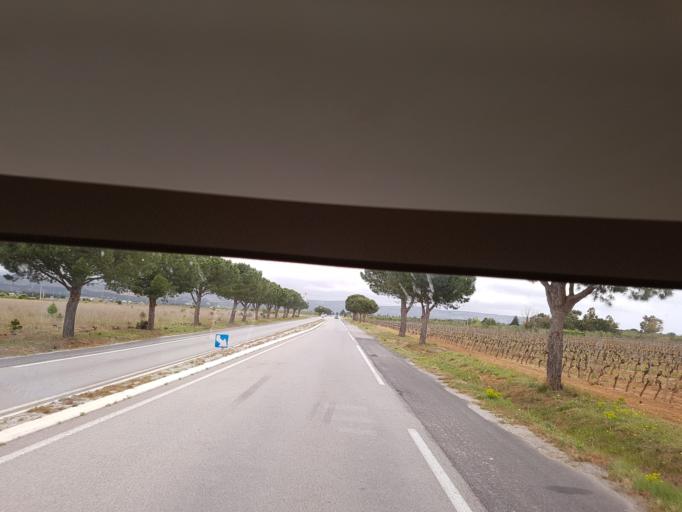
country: FR
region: Languedoc-Roussillon
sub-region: Departement des Pyrenees-Orientales
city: Salses-le-Chateau
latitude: 42.8068
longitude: 2.9120
